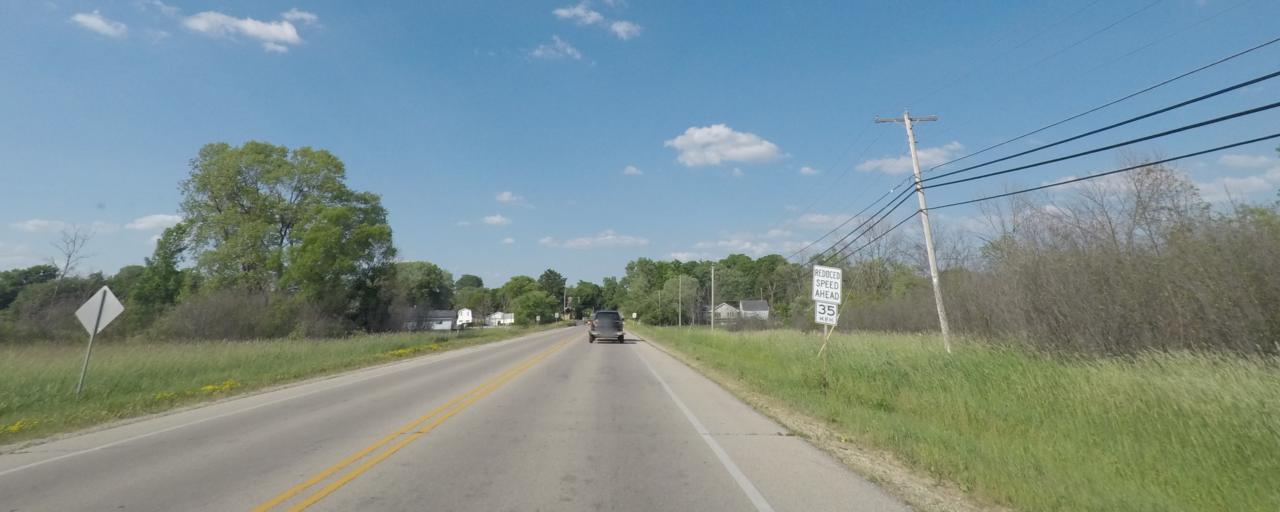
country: US
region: Wisconsin
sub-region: Waukesha County
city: Big Bend
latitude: 42.8749
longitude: -88.2124
